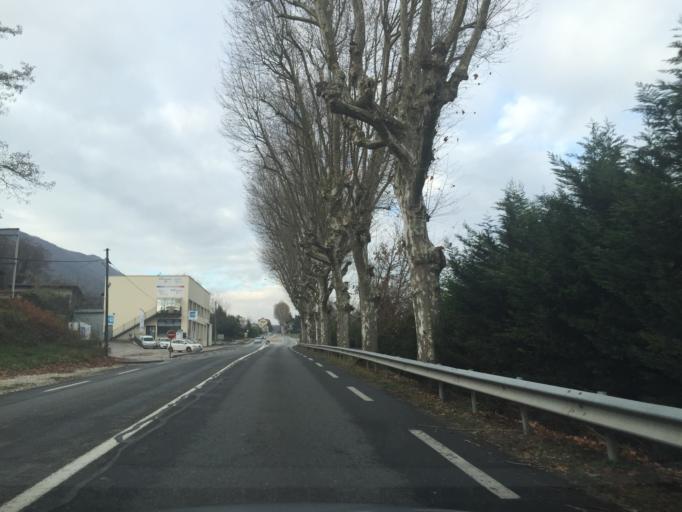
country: FR
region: Rhone-Alpes
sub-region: Departement de la Savoie
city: Gresy-sur-Aix
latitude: 45.7173
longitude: 5.9177
